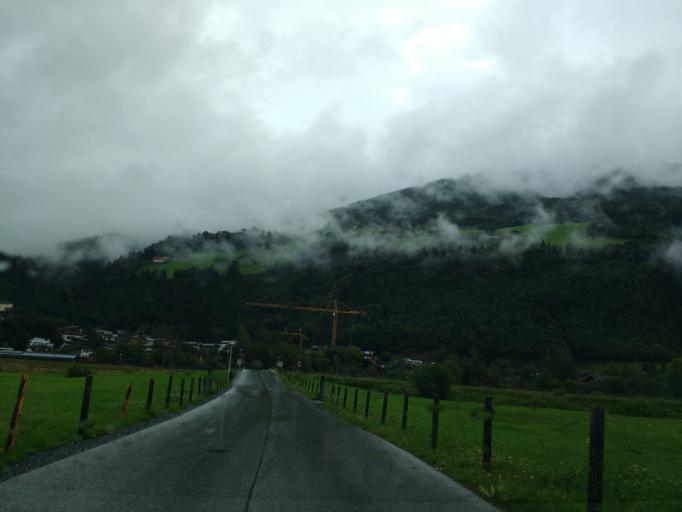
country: AT
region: Salzburg
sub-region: Politischer Bezirk Zell am See
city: Neukirchen am Grossvenediger
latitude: 47.2507
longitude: 12.2852
